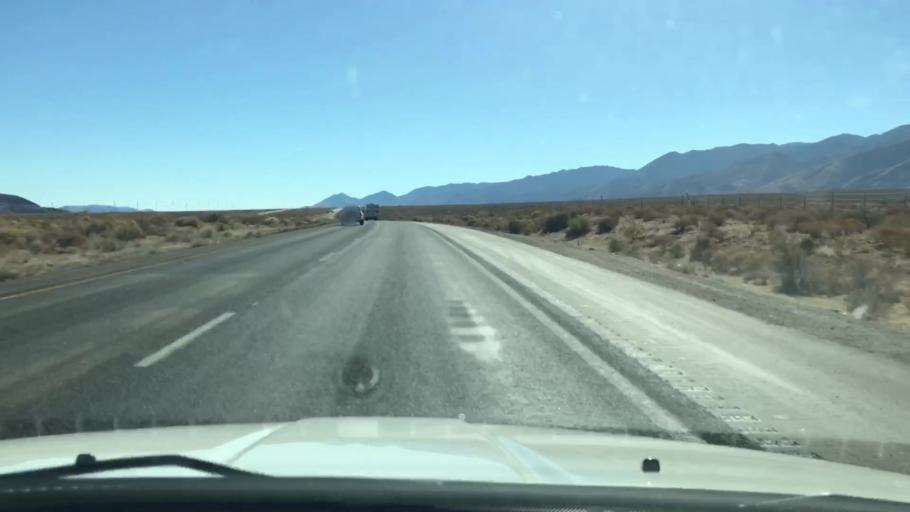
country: US
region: California
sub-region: Inyo County
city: Lone Pine
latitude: 36.1655
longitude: -117.9778
